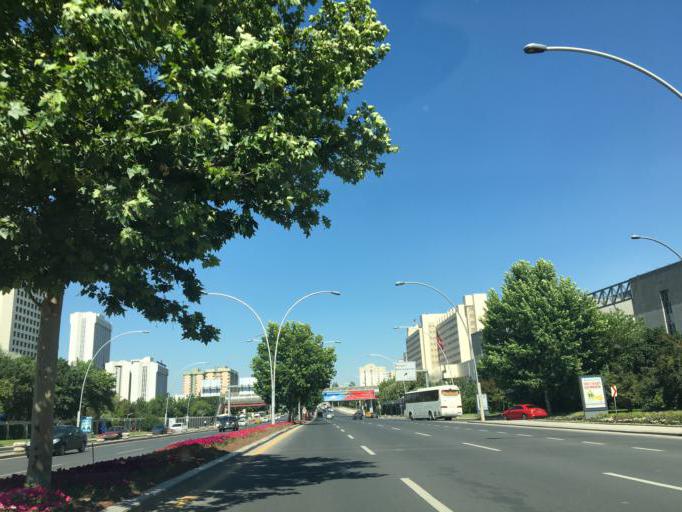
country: TR
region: Ankara
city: Ankara
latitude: 39.9130
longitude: 32.8158
